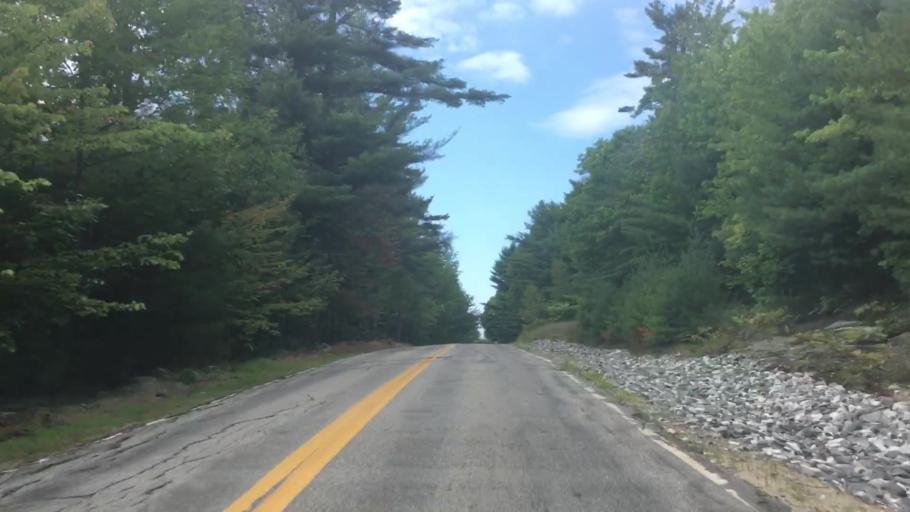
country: US
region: Maine
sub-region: Oxford County
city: Oxford
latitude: 44.0736
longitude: -70.5461
